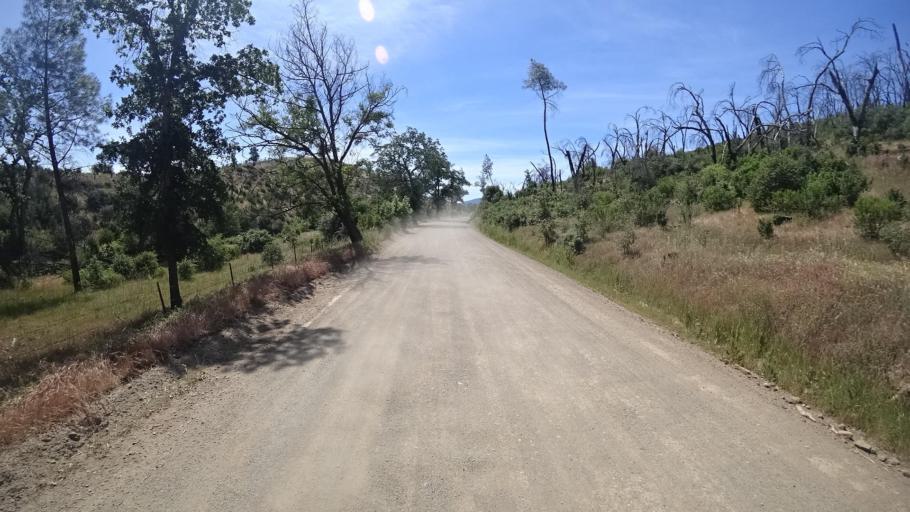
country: US
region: California
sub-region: Lake County
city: Middletown
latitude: 38.8048
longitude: -122.6152
